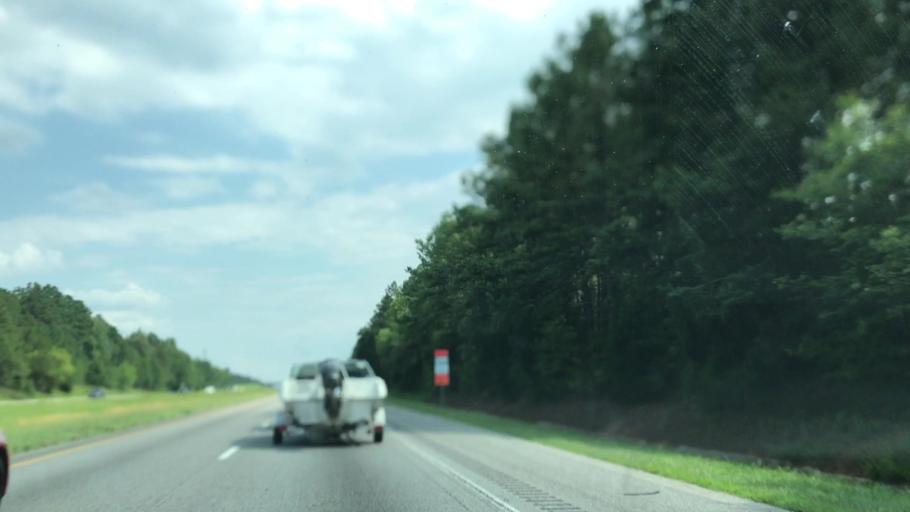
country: US
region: South Carolina
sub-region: Chester County
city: Great Falls
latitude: 34.6187
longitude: -81.0214
